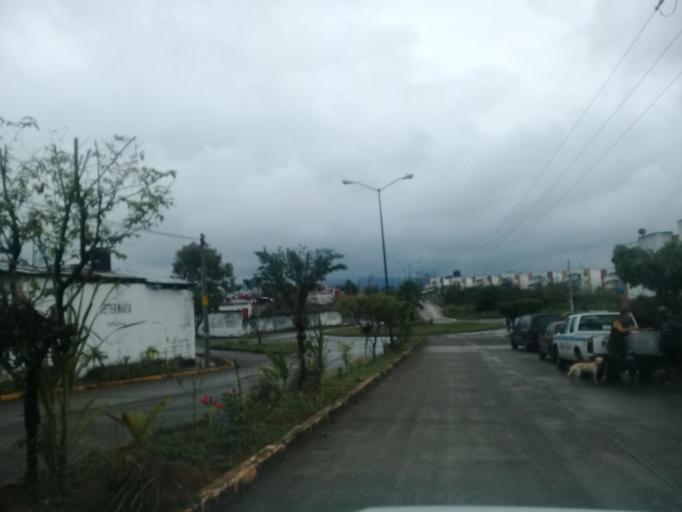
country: MX
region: Veracruz
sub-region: Cordoba
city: San Jose de Tapia
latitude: 18.8375
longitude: -96.9552
